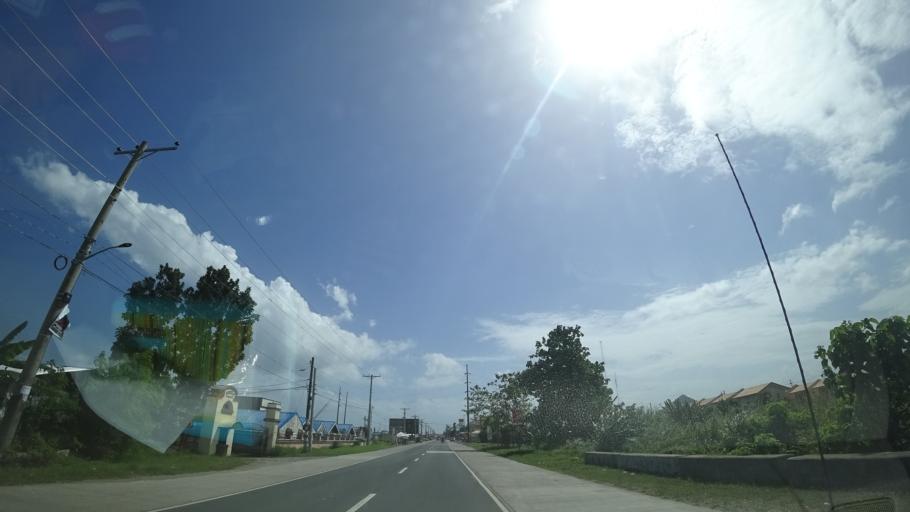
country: PH
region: Eastern Visayas
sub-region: Province of Leyte
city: Pawing
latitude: 11.1889
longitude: 124.9947
